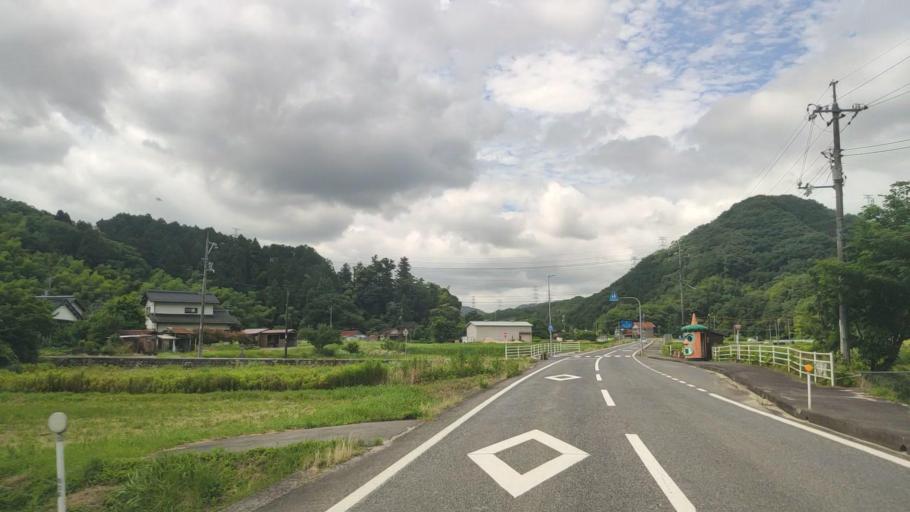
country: JP
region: Tottori
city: Yonago
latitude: 35.3000
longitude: 133.4152
